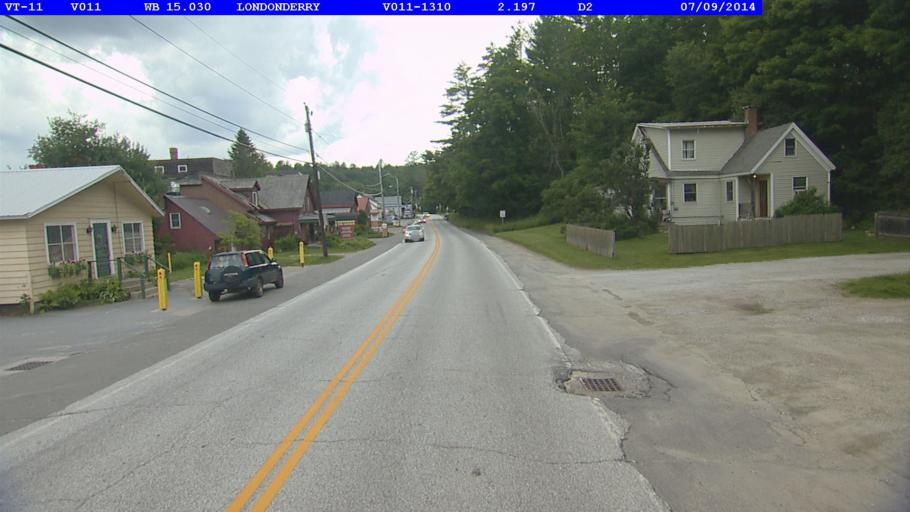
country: US
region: Vermont
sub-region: Windsor County
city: Chester
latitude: 43.2280
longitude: -72.8104
